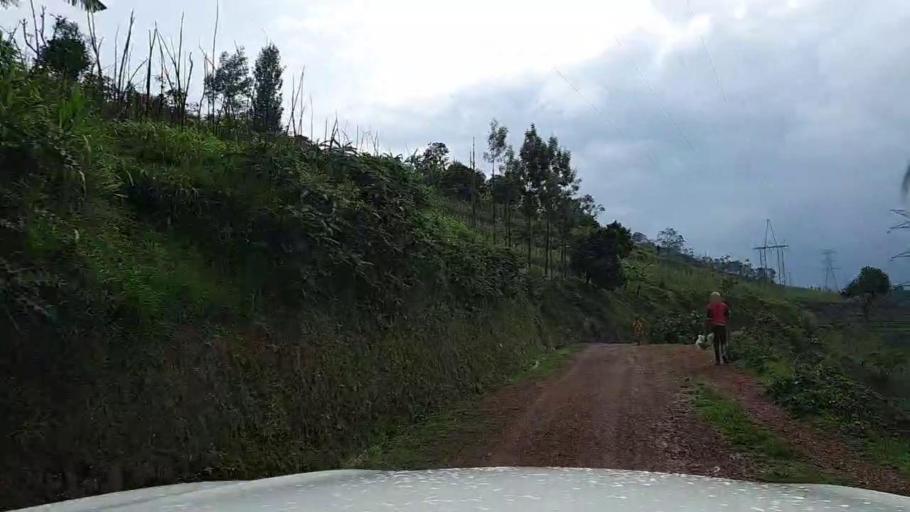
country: RW
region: Northern Province
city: Byumba
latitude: -1.7199
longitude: 29.9066
